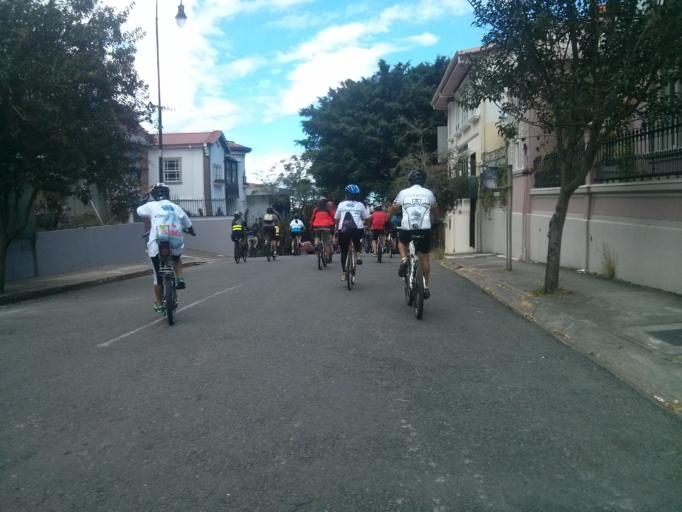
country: CR
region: San Jose
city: San Jose
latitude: 9.9374
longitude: -84.0734
